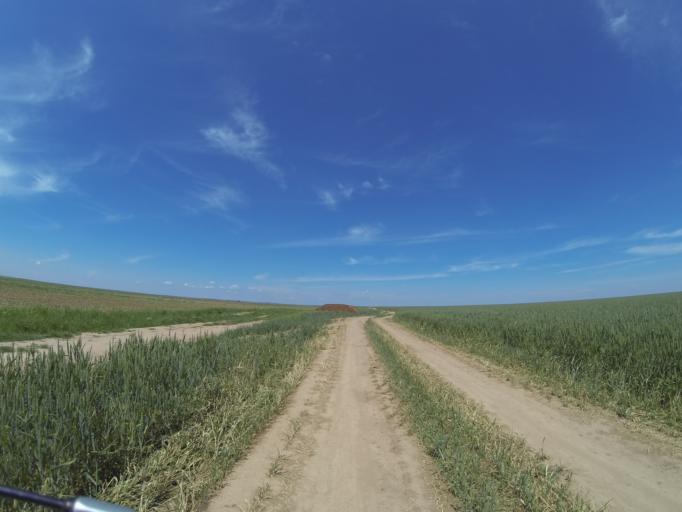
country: RO
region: Dolj
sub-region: Comuna Teslui
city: Teslui
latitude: 44.1802
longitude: 24.1711
